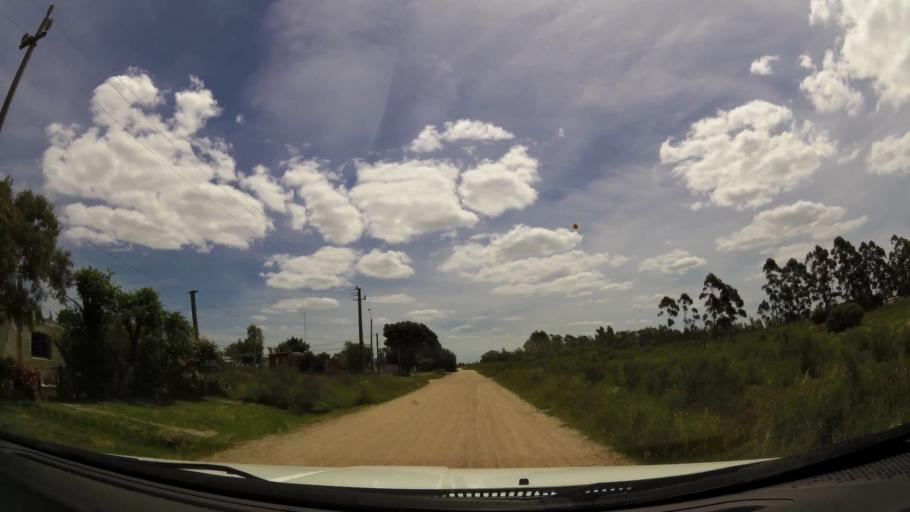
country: UY
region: San Jose
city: Delta del Tigre
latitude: -34.7509
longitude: -56.4225
